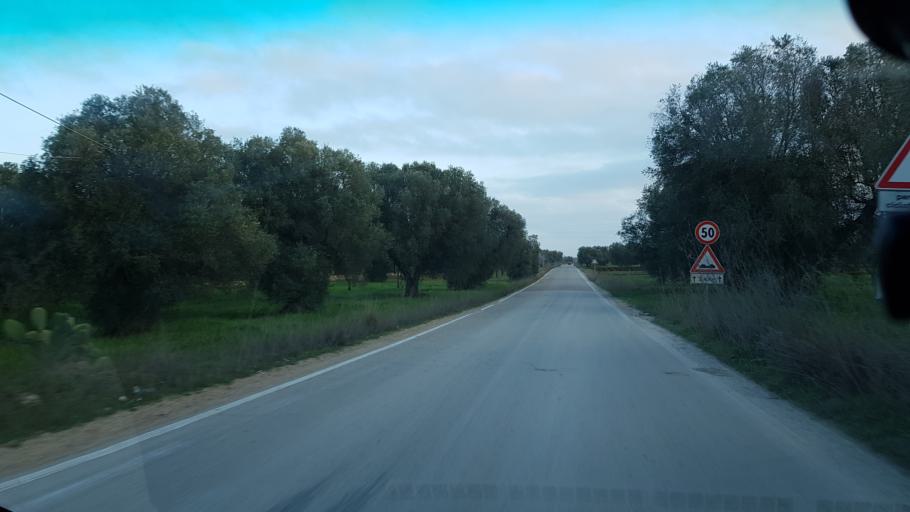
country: IT
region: Apulia
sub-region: Provincia di Brindisi
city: San Vito dei Normanni
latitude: 40.6412
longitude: 17.7788
